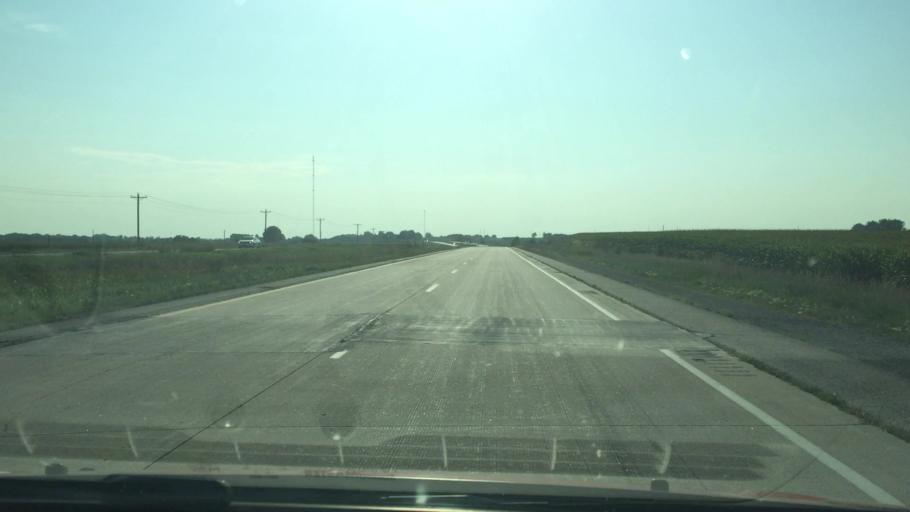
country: US
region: Iowa
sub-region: Cedar County
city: Durant
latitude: 41.5194
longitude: -90.8666
